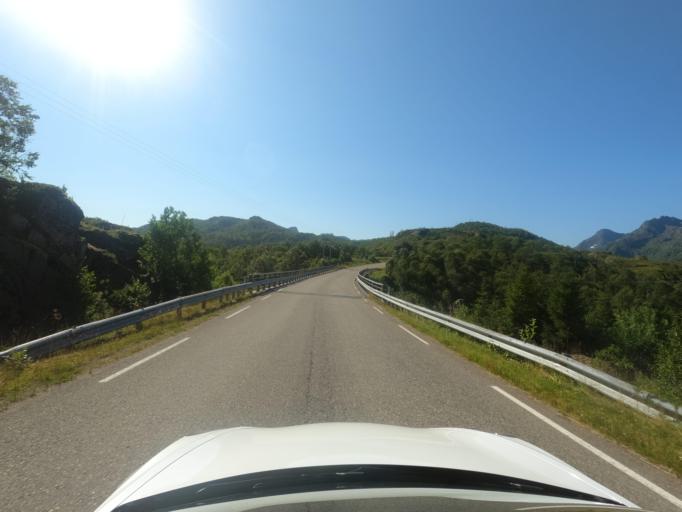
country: NO
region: Nordland
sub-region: Hadsel
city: Stokmarknes
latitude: 68.4366
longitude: 15.1828
